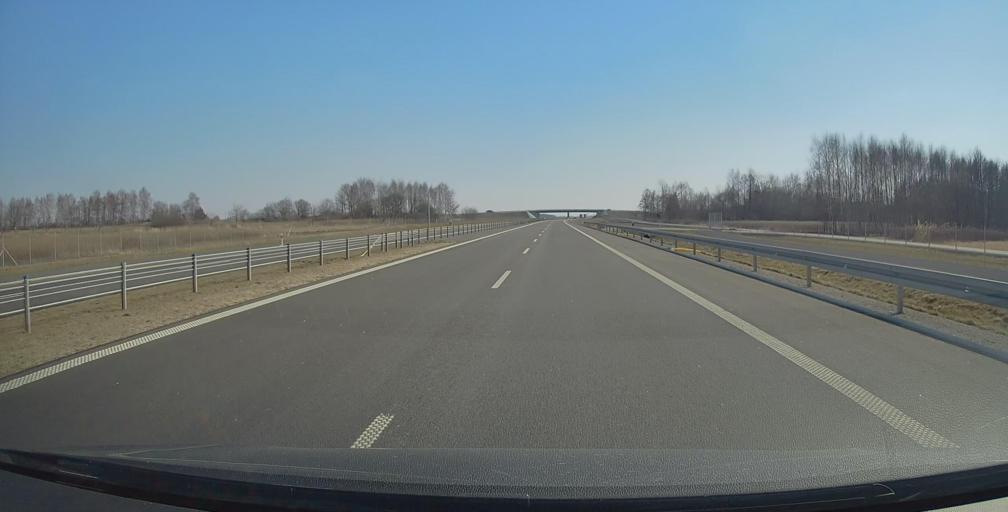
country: PL
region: Lublin Voivodeship
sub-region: Powiat janowski
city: Modliborzyce
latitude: 50.7385
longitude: 22.3307
